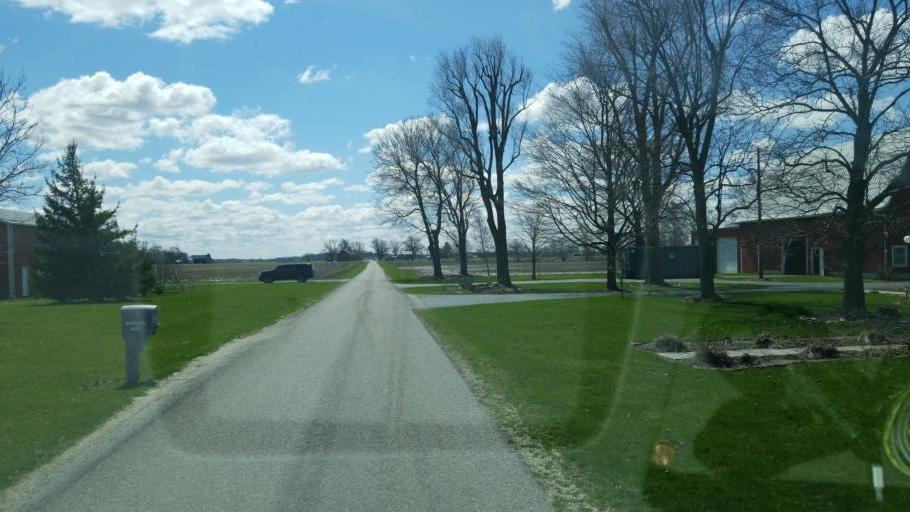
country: US
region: Ohio
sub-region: Hancock County
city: Findlay
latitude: 41.0183
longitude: -83.5109
